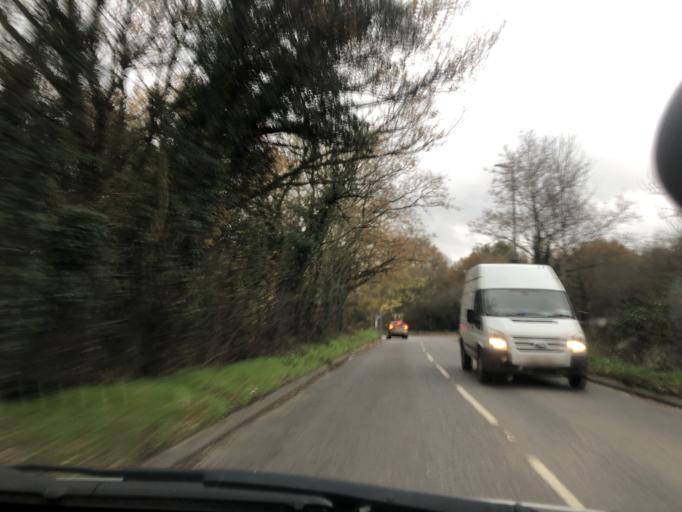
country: GB
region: England
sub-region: Greater London
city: Bexley
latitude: 51.4404
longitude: 0.1821
